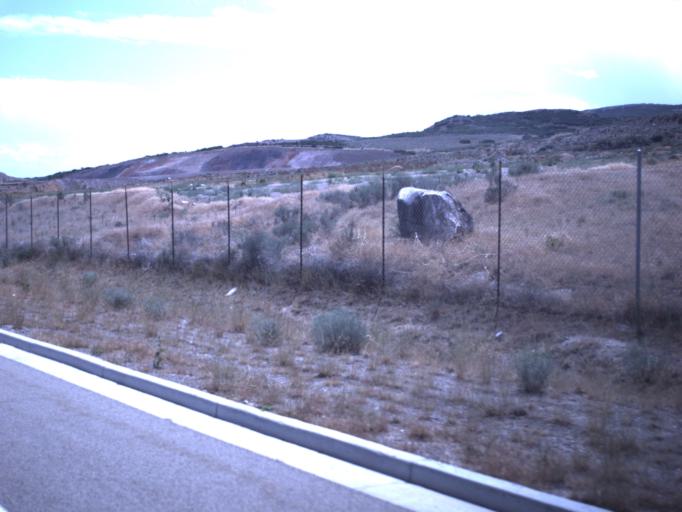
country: US
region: Utah
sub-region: Salt Lake County
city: Bluffdale
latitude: 40.4673
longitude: -111.9626
